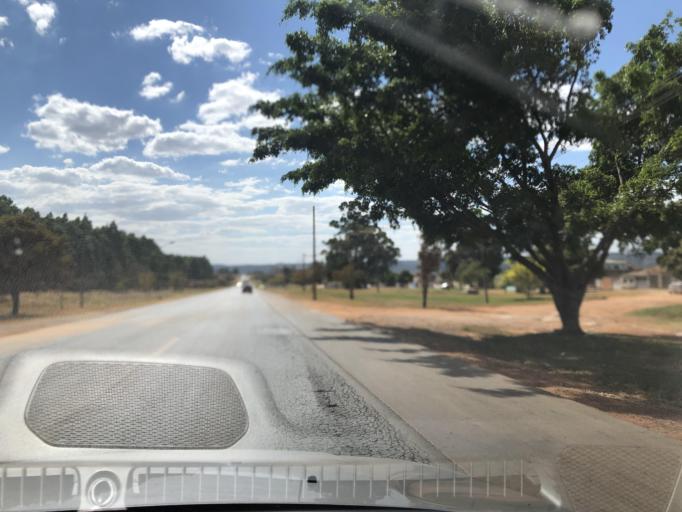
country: BR
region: Federal District
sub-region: Brasilia
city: Brasilia
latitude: -15.8921
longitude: -48.1499
